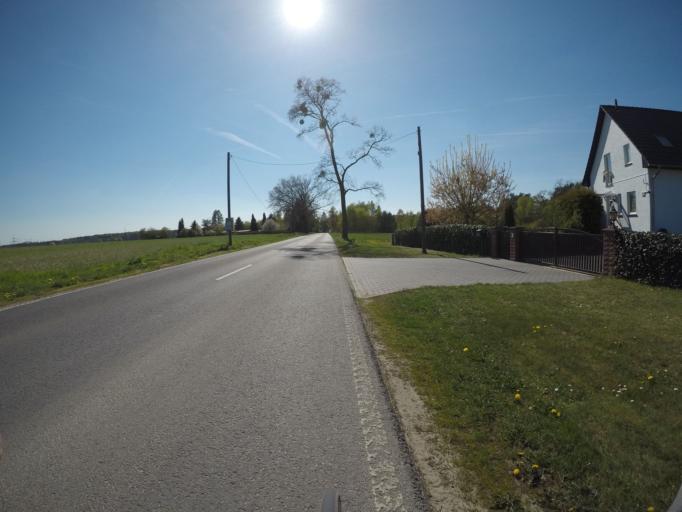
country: DE
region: Brandenburg
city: Rehfelde
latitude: 52.5547
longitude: 13.9482
